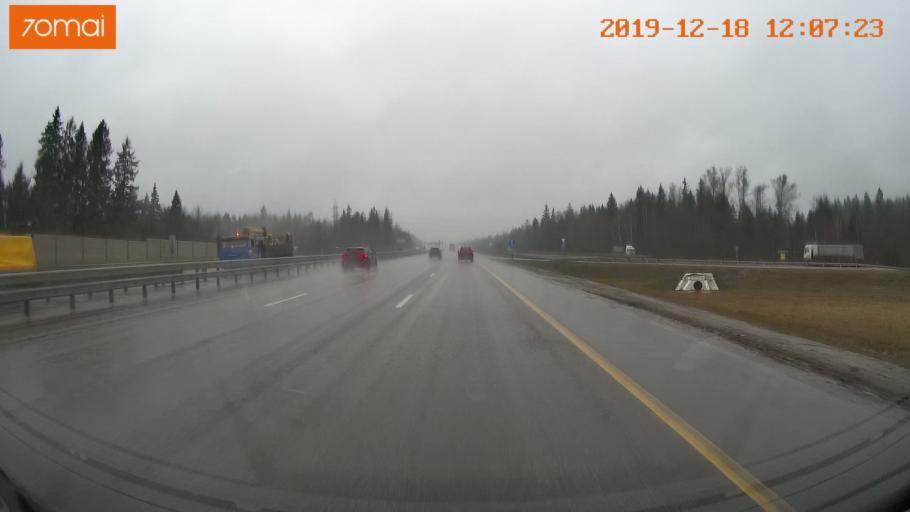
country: RU
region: Moskovskaya
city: Kostrovo
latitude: 55.8897
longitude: 36.6552
